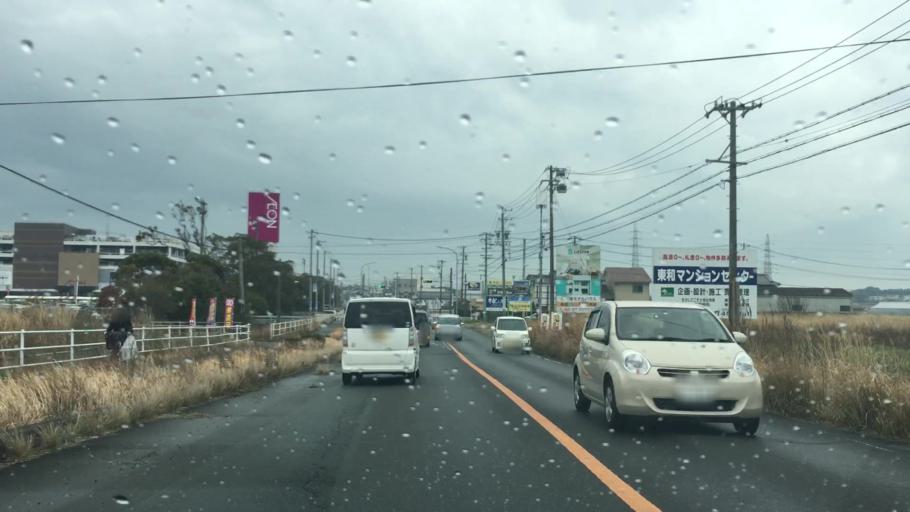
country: JP
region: Aichi
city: Toyohashi
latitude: 34.7115
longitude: 137.3864
